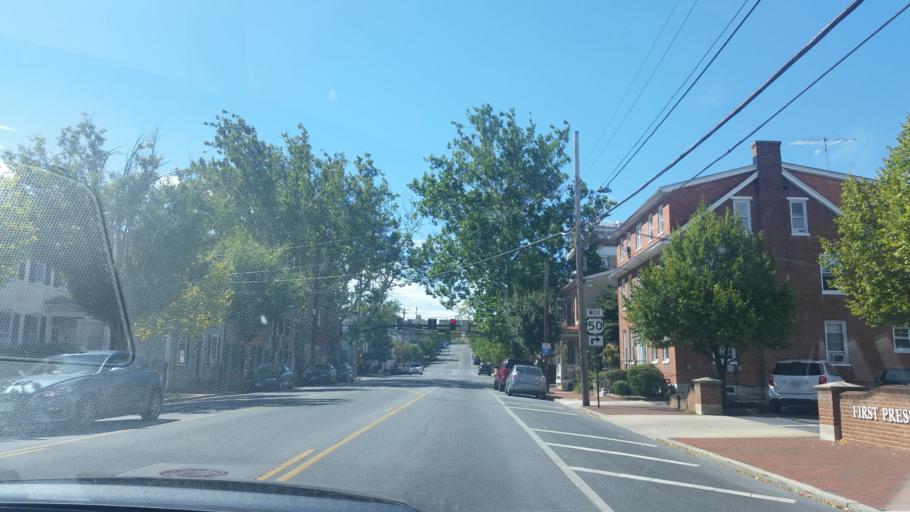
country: US
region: Virginia
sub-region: City of Winchester
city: Winchester
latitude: 39.1826
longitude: -78.1646
